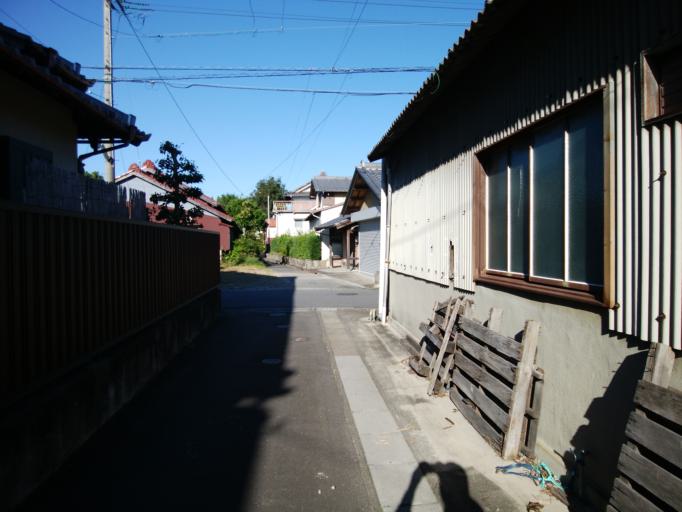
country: JP
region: Aichi
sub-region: Aisai-shi
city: Aisai
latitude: 35.1576
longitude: 136.7515
